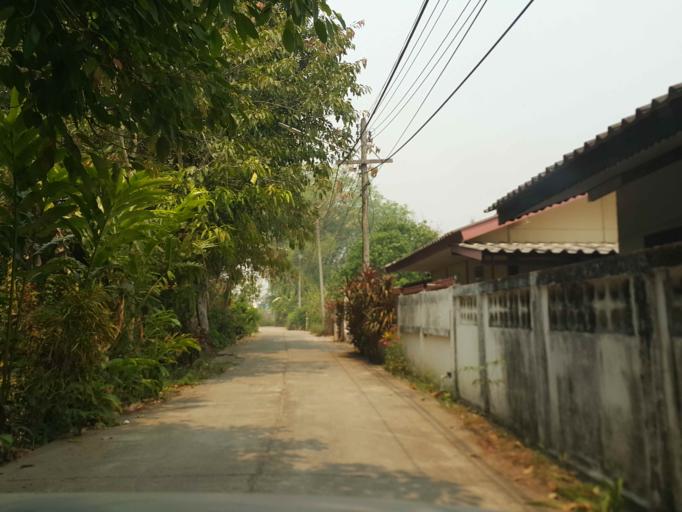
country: TH
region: Chiang Mai
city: Mae Taeng
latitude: 19.0741
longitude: 98.9396
